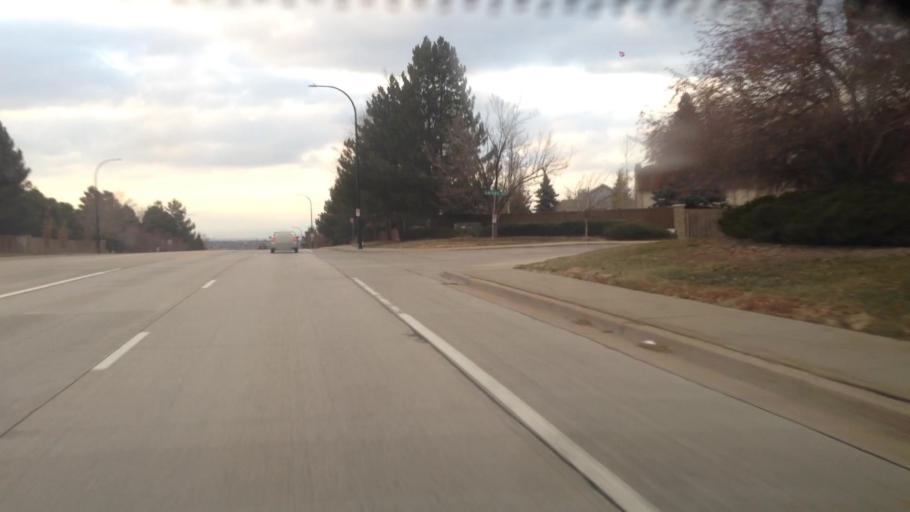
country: US
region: Colorado
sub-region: Douglas County
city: Carriage Club
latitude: 39.5380
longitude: -104.9082
